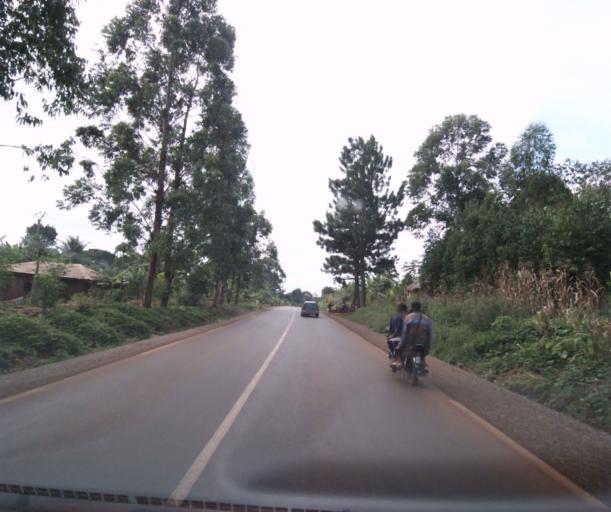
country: CM
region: West
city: Mbouda
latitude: 5.5880
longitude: 10.2962
